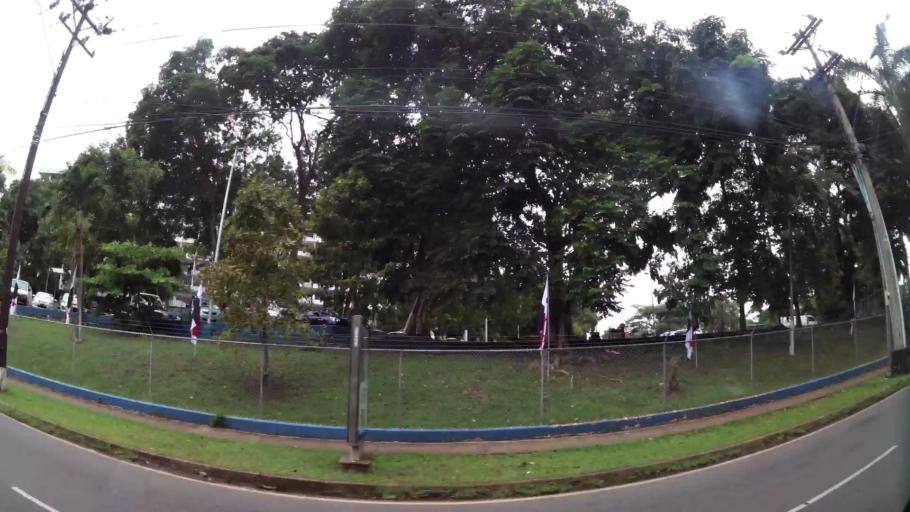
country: PA
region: Panama
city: Panama
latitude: 8.9818
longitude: -79.5358
